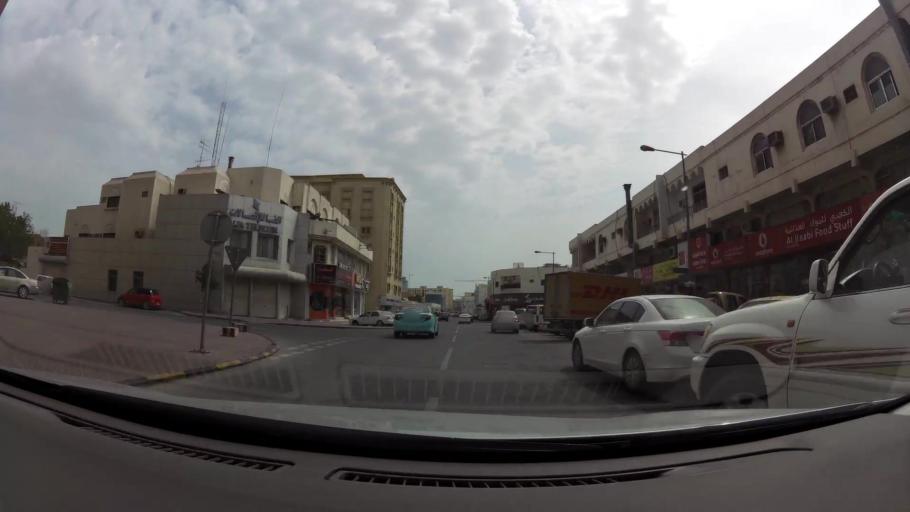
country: QA
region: Baladiyat ad Dawhah
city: Doha
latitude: 25.2822
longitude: 51.4973
